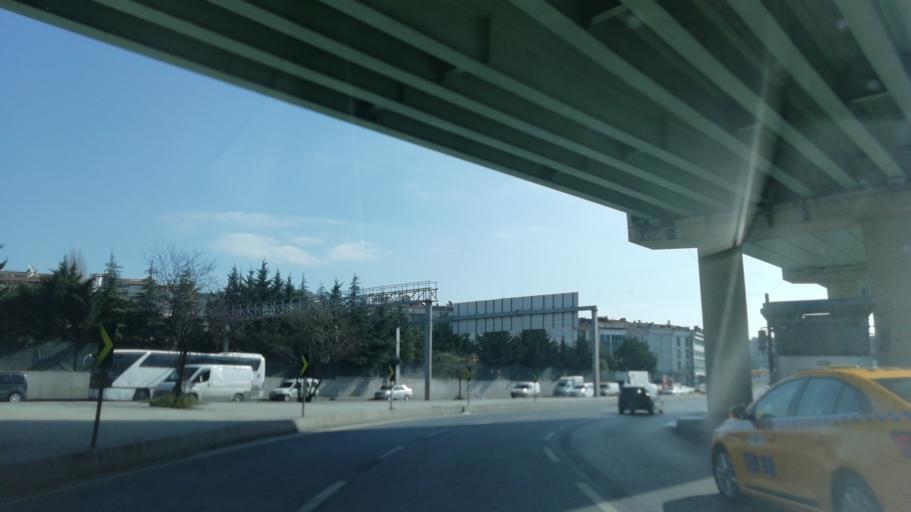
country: TR
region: Istanbul
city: Esenler
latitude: 41.0355
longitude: 28.8945
